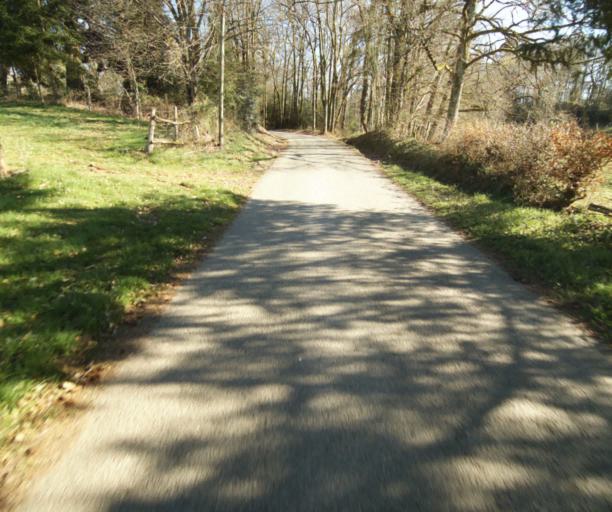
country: FR
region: Limousin
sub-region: Departement de la Correze
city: Chamboulive
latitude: 45.4743
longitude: 1.6972
